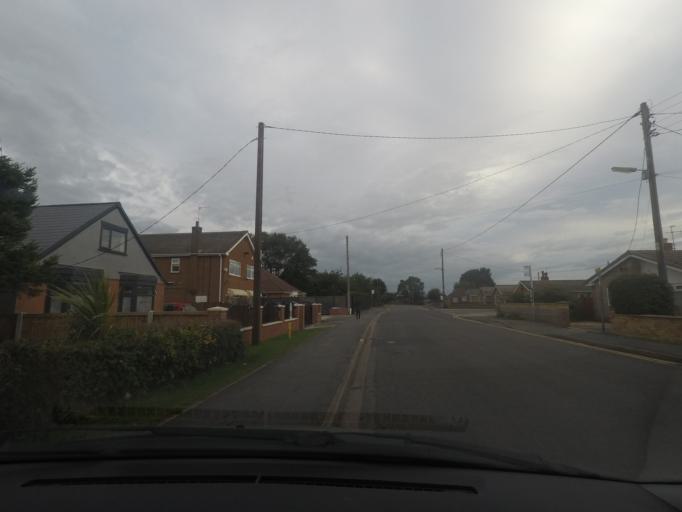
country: GB
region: England
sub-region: Lincolnshire
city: Chapel Saint Leonards
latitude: 53.2206
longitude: 0.3361
